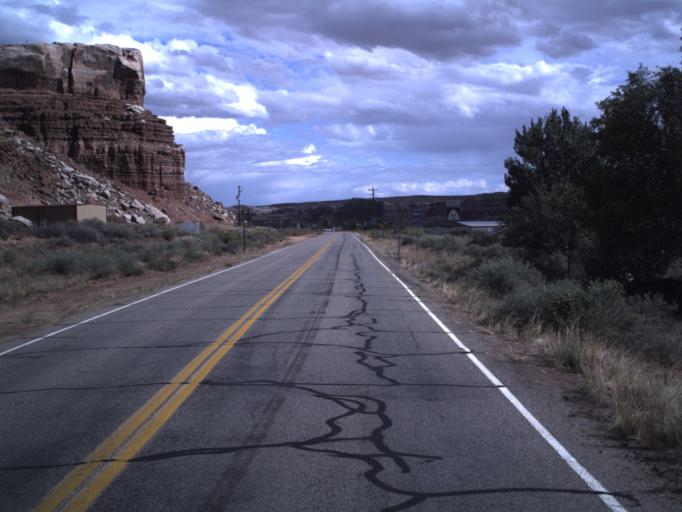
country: US
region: Utah
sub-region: San Juan County
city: Blanding
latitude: 37.2864
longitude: -109.5450
